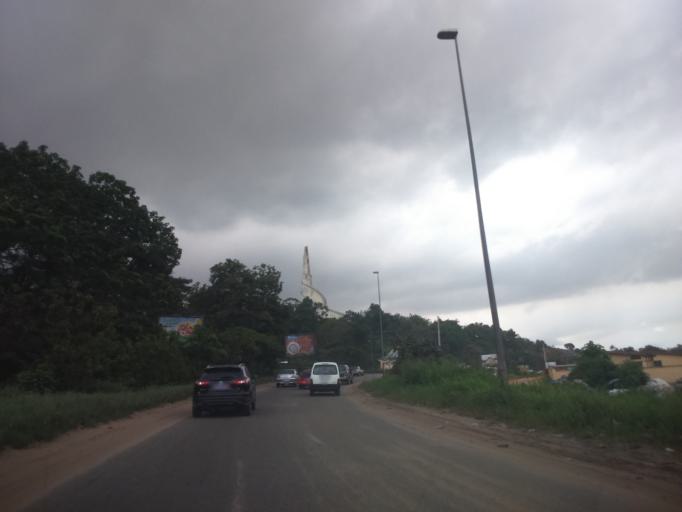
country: CI
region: Lagunes
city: Abidjan
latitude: 5.3594
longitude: -4.0413
